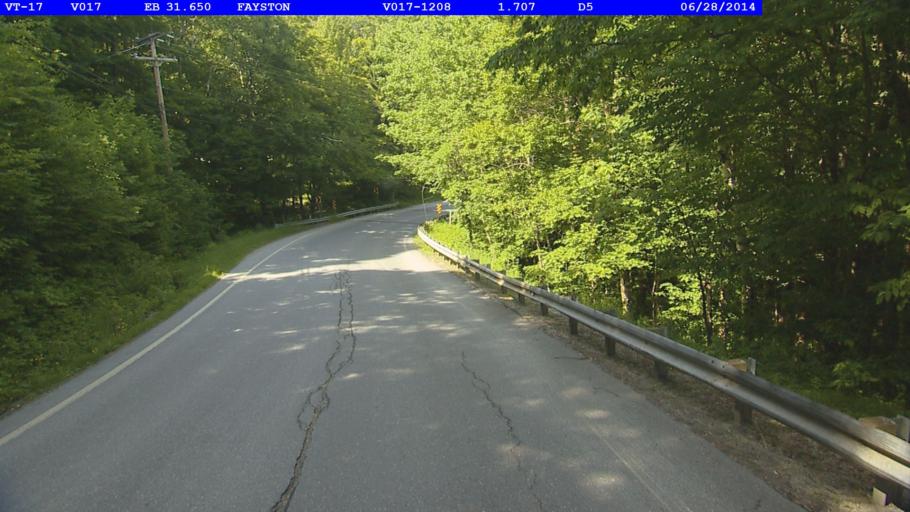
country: US
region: Vermont
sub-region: Addison County
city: Bristol
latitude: 44.2035
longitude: -72.9084
